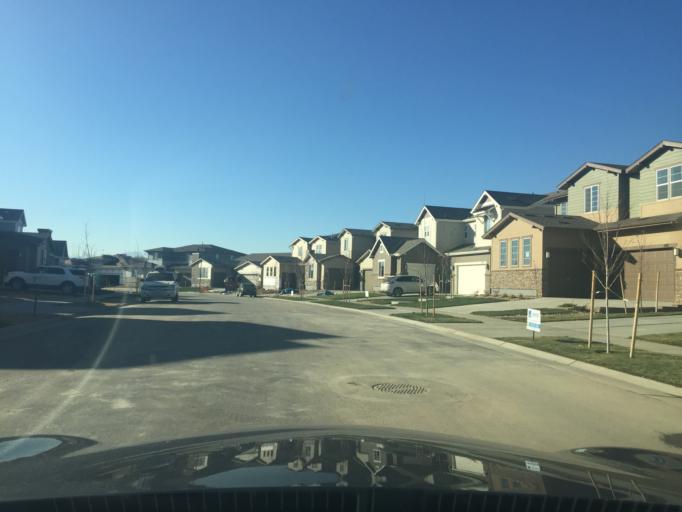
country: US
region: Colorado
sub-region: Boulder County
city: Erie
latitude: 40.0509
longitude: -105.0349
